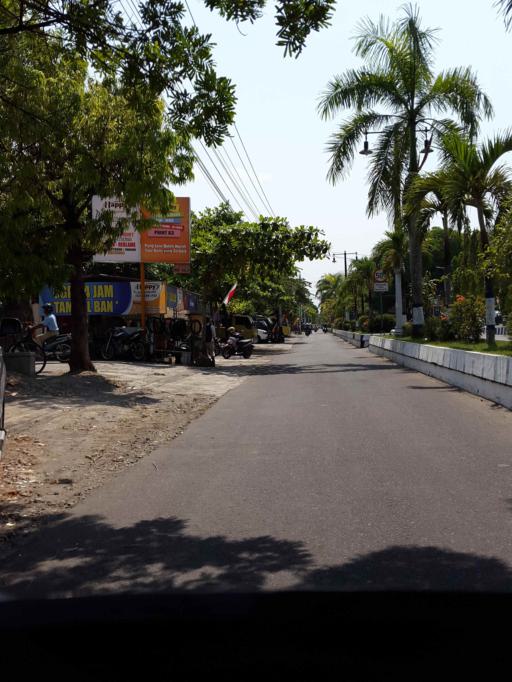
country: ID
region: Central Java
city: Jaten
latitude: -7.5926
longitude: 110.9376
